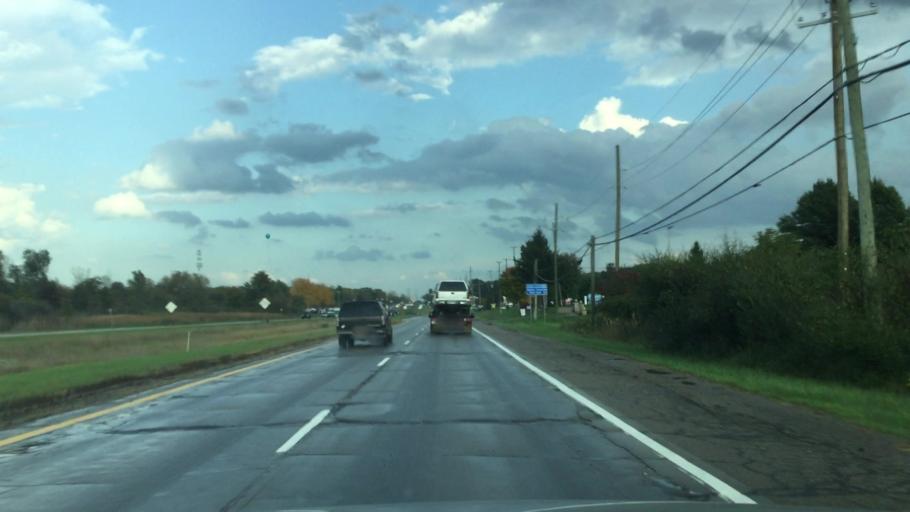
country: US
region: Michigan
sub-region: Oakland County
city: Milford
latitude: 42.6359
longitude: -83.6683
